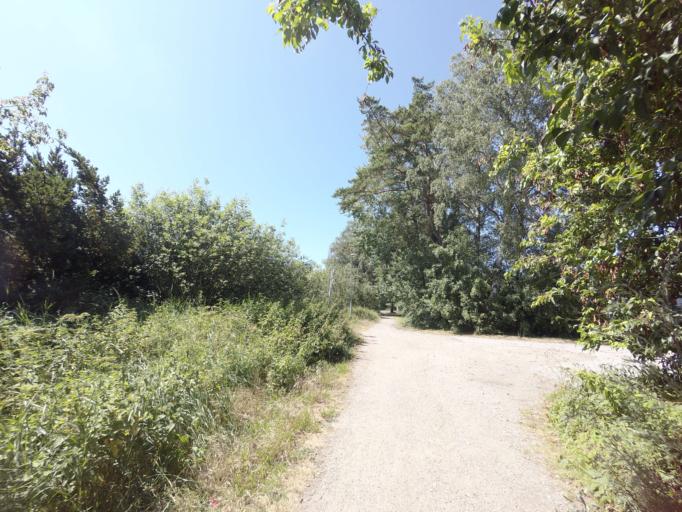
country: SE
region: Skane
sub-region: Vellinge Kommun
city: Skanor med Falsterbo
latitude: 55.4050
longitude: 12.8507
